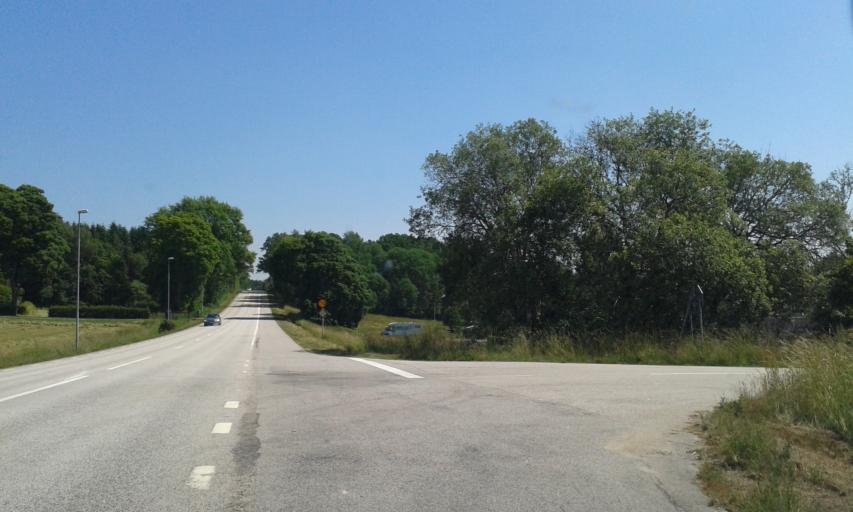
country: SE
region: Blekinge
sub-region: Karlskrona Kommun
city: Rodeby
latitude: 56.2737
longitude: 15.5351
